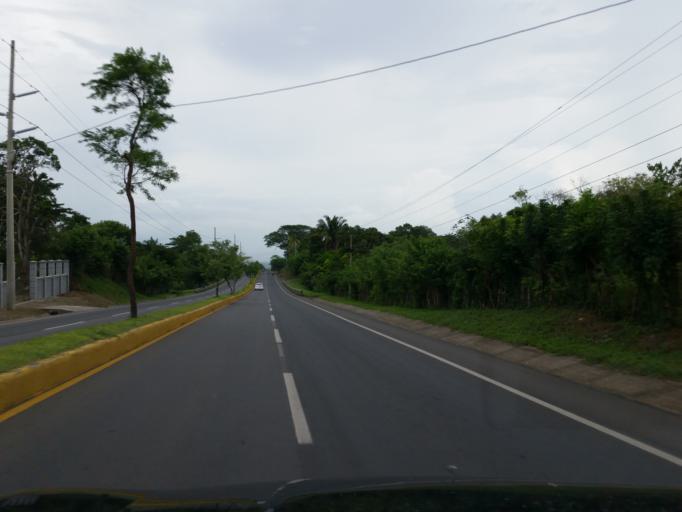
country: NI
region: Masaya
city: Masaya
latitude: 11.9750
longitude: -86.0624
